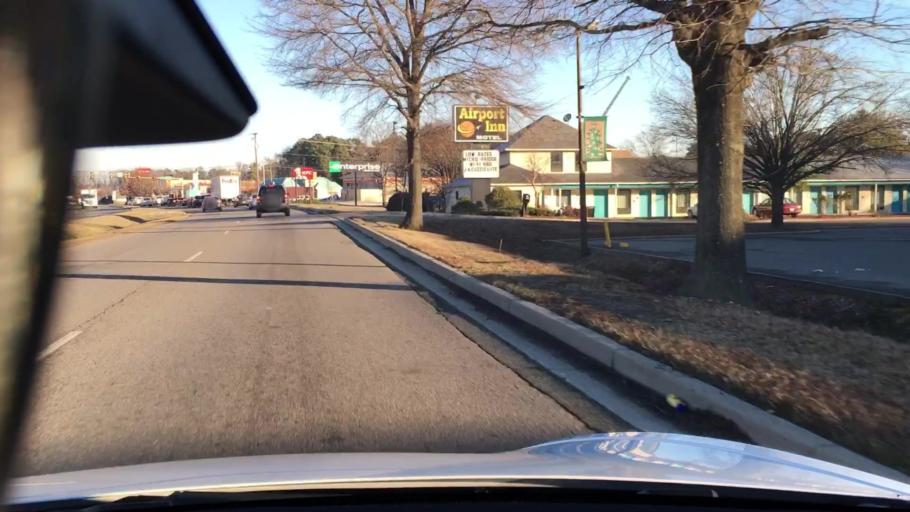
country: US
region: Virginia
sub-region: Henrico County
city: Fort Lee
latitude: 37.5154
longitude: -77.3496
